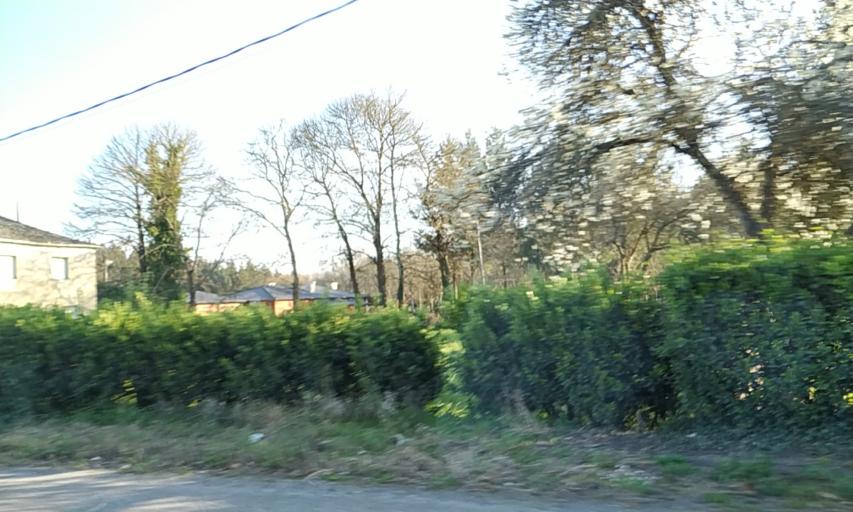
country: ES
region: Galicia
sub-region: Provincia de Lugo
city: Corgo
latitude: 42.9507
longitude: -7.4553
